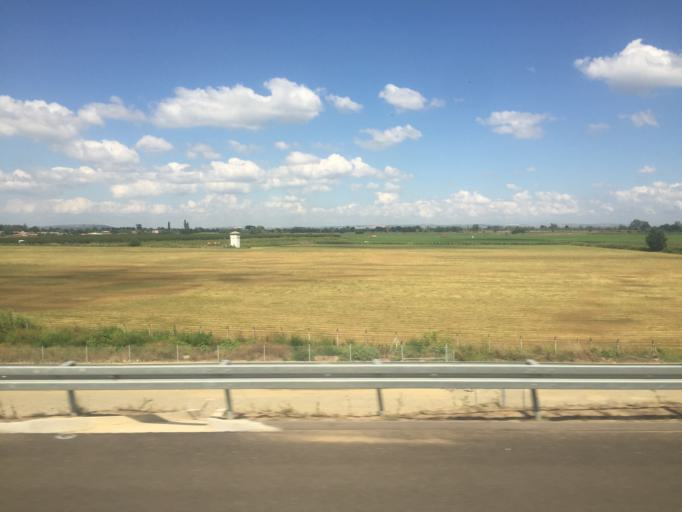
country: TR
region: Bursa
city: Tatkavakli
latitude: 40.0773
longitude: 28.2564
